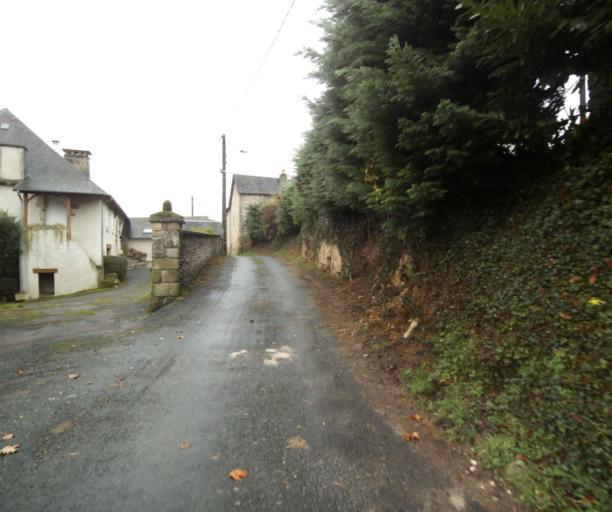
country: FR
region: Limousin
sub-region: Departement de la Correze
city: Cornil
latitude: 45.1867
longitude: 1.6330
